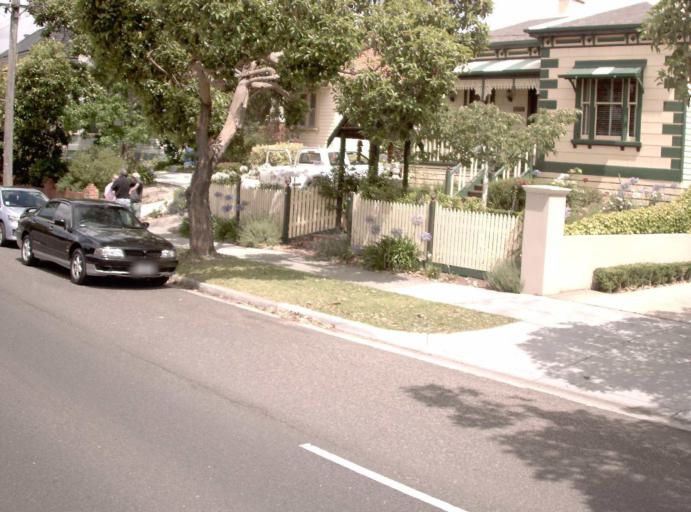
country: AU
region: Victoria
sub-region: Boroondara
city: Kew East
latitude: -37.8002
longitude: 145.0578
